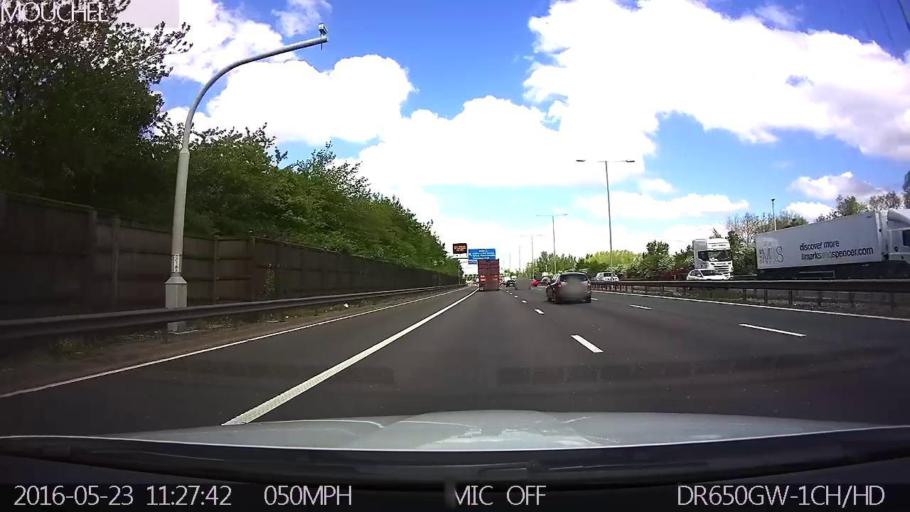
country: GB
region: England
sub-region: Walsall
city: Bloxwich
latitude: 52.6168
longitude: -2.0301
